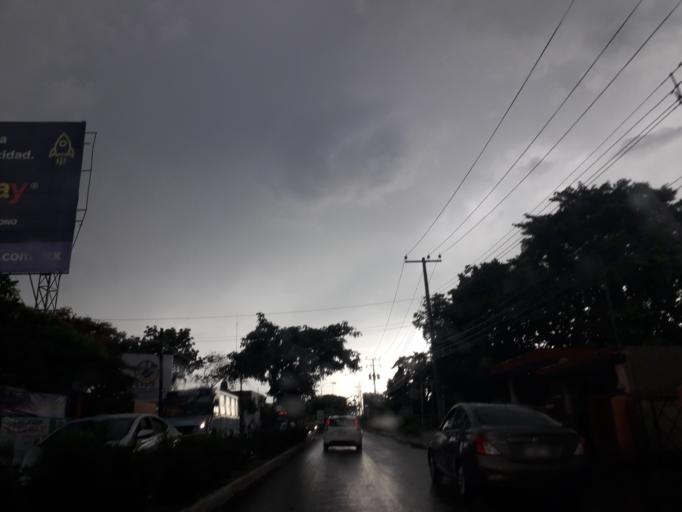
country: MX
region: Yucatan
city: Merida
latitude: 20.9761
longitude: -89.6417
